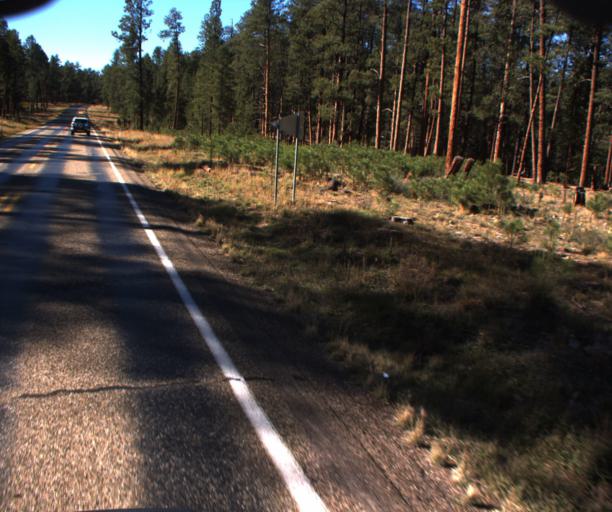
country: US
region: Arizona
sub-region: Coconino County
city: Fredonia
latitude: 36.7212
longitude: -112.2016
